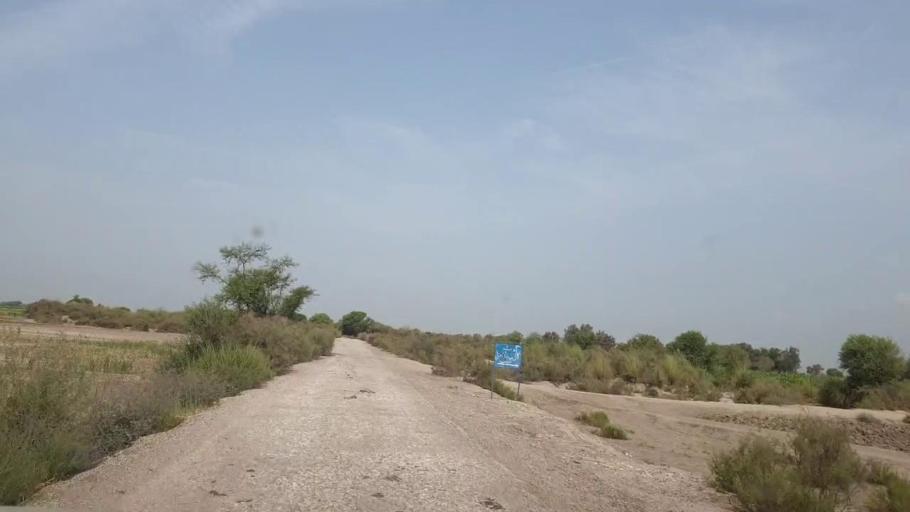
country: PK
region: Sindh
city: Sobhadero
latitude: 27.3938
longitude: 68.2636
